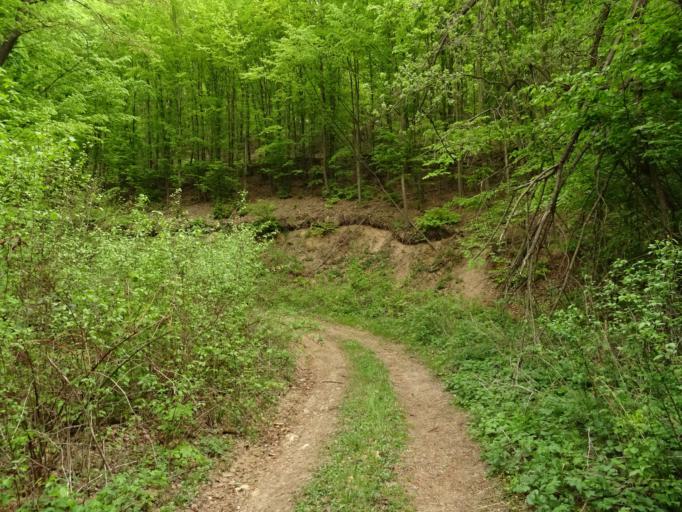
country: HU
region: Borsod-Abauj-Zemplen
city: Satoraljaujhely
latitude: 48.4080
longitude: 21.6171
